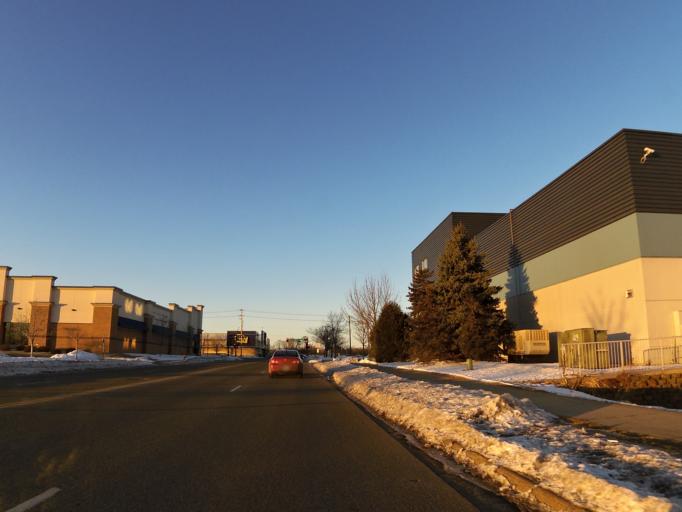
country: US
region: Minnesota
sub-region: Ramsey County
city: North Saint Paul
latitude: 45.0344
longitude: -93.0257
